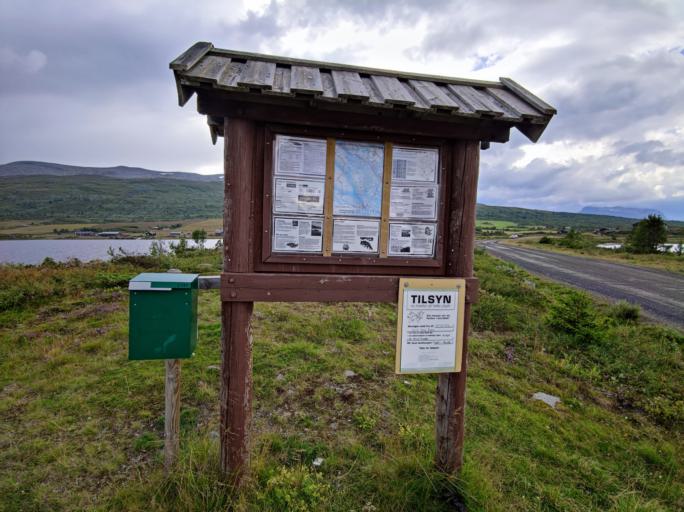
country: NO
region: Oppland
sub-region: Vang
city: Vang
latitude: 61.0763
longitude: 8.7277
